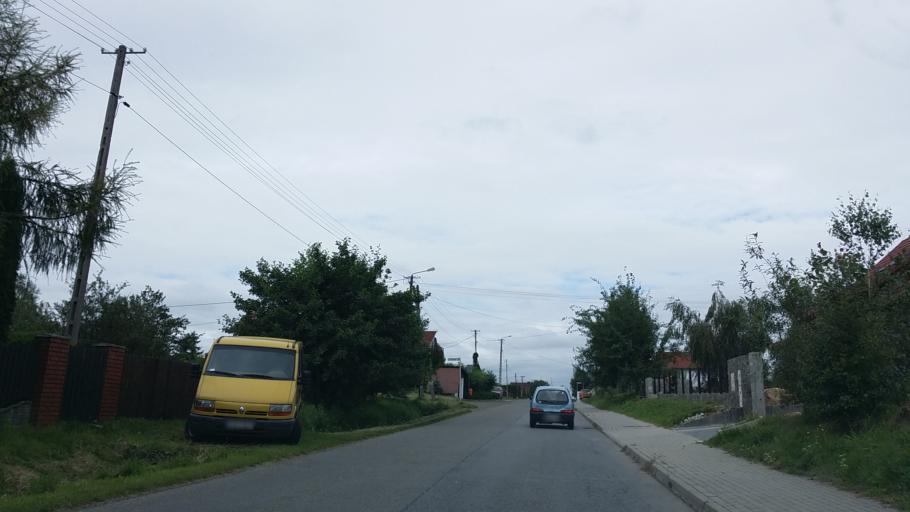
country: PL
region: Lesser Poland Voivodeship
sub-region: Powiat wadowicki
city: Tomice
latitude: 49.8987
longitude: 19.4680
